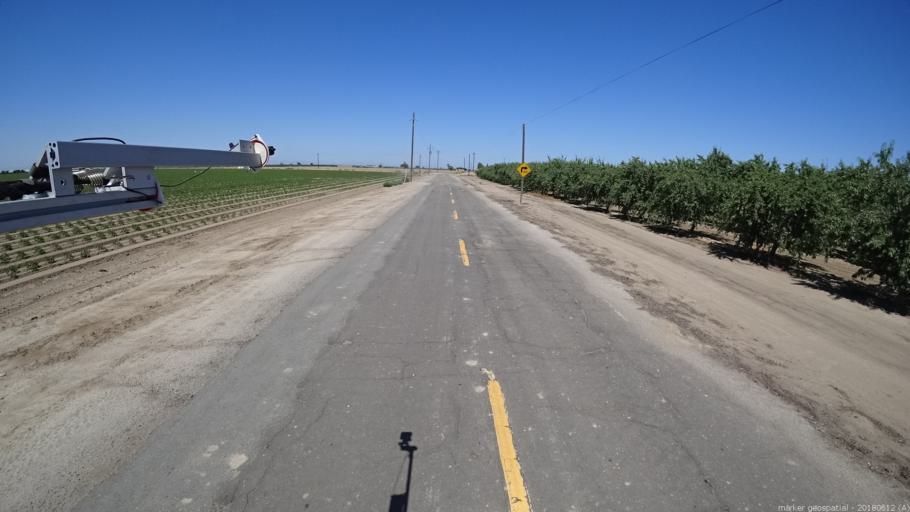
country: US
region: California
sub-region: Madera County
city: Chowchilla
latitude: 37.0254
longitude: -120.3395
